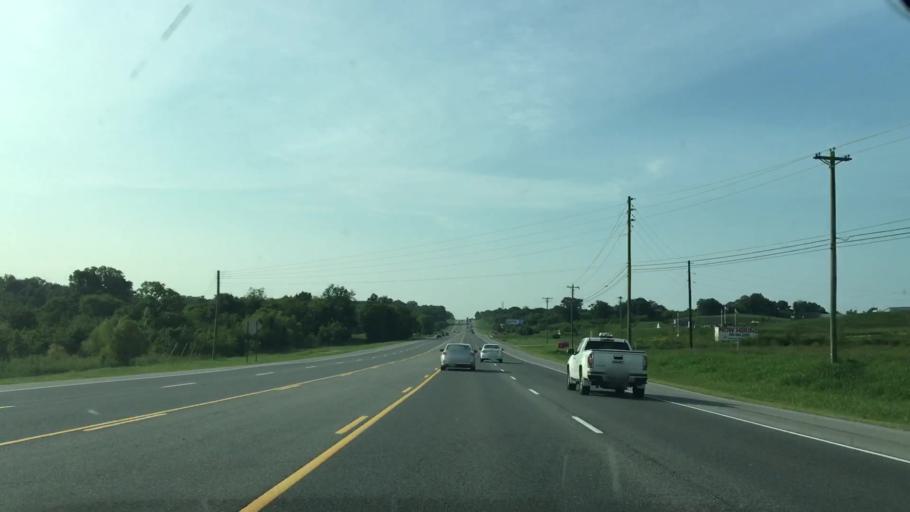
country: US
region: Tennessee
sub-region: Wilson County
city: Mount Juliet
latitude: 36.2233
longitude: -86.4254
